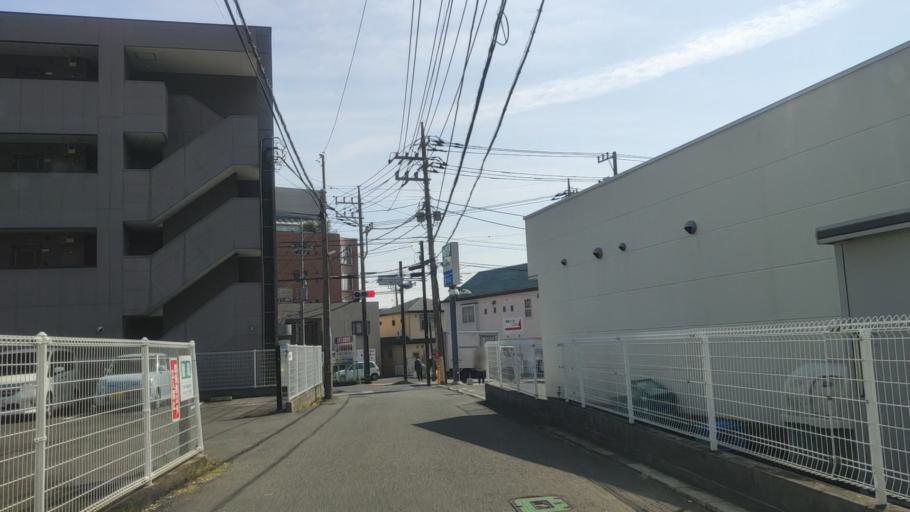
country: JP
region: Kanagawa
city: Isehara
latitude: 35.3829
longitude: 139.2784
